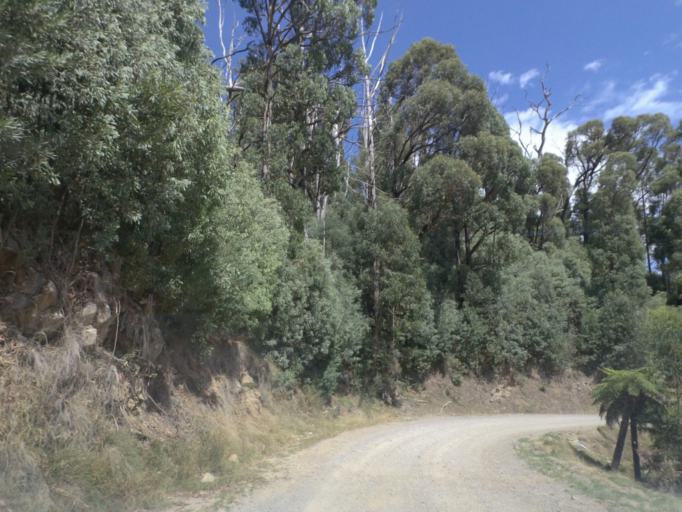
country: AU
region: Victoria
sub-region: Murrindindi
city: Alexandra
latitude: -37.4556
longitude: 145.7867
